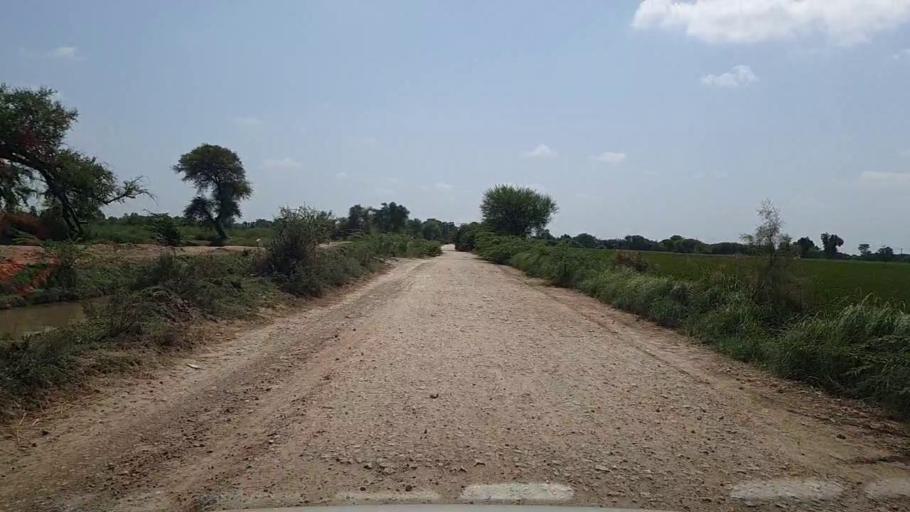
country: PK
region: Sindh
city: Kario
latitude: 24.8620
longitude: 68.6868
